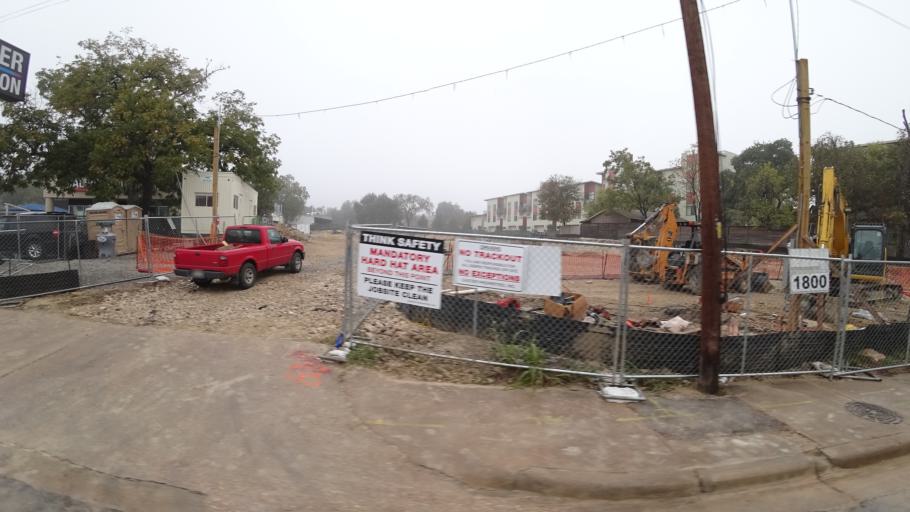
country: US
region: Texas
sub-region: Travis County
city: Austin
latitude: 30.2502
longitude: -97.7664
